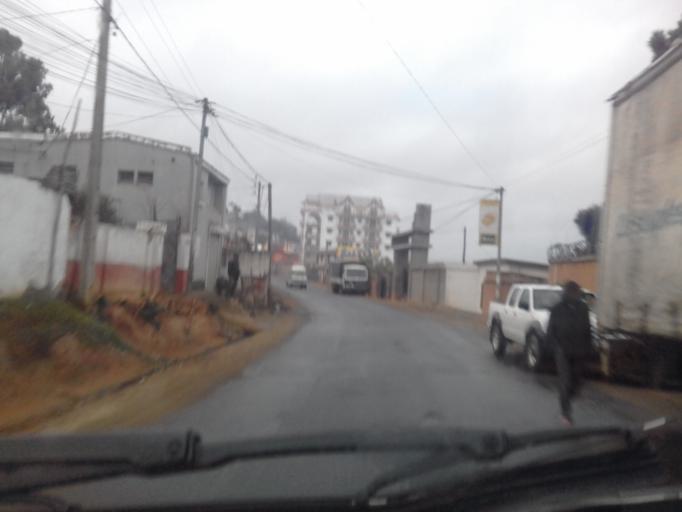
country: MG
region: Analamanga
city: Antananarivo
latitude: -18.8678
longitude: 47.5511
